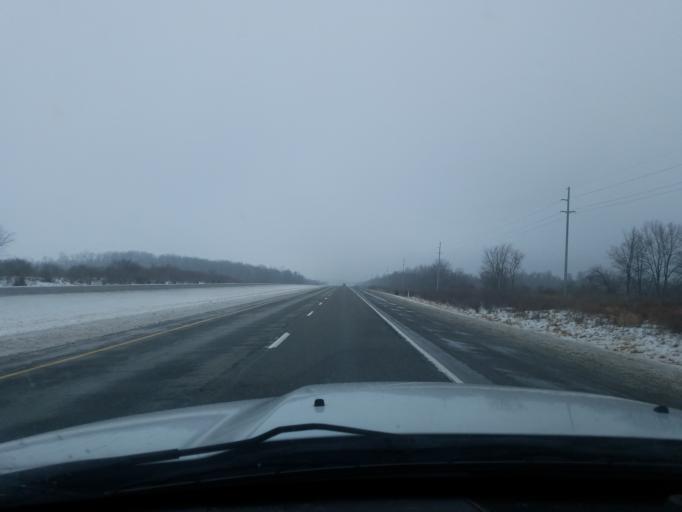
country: US
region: Indiana
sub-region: Fulton County
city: Rochester
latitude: 41.0148
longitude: -86.1706
